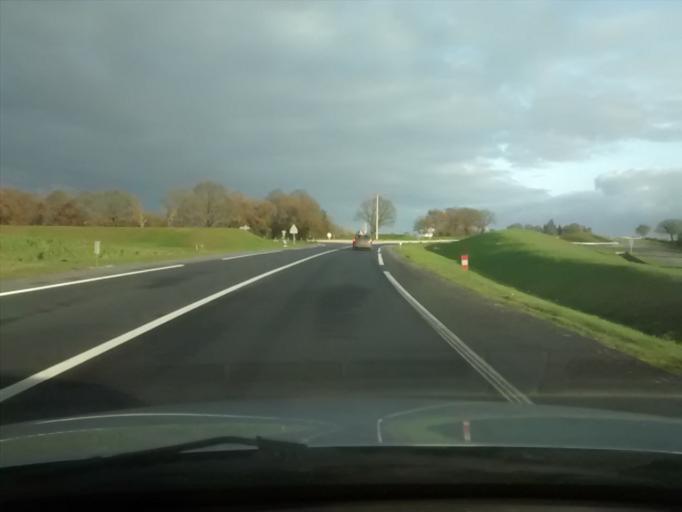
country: FR
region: Pays de la Loire
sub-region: Departement de la Mayenne
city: Loiron
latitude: 48.0738
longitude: -0.9144
